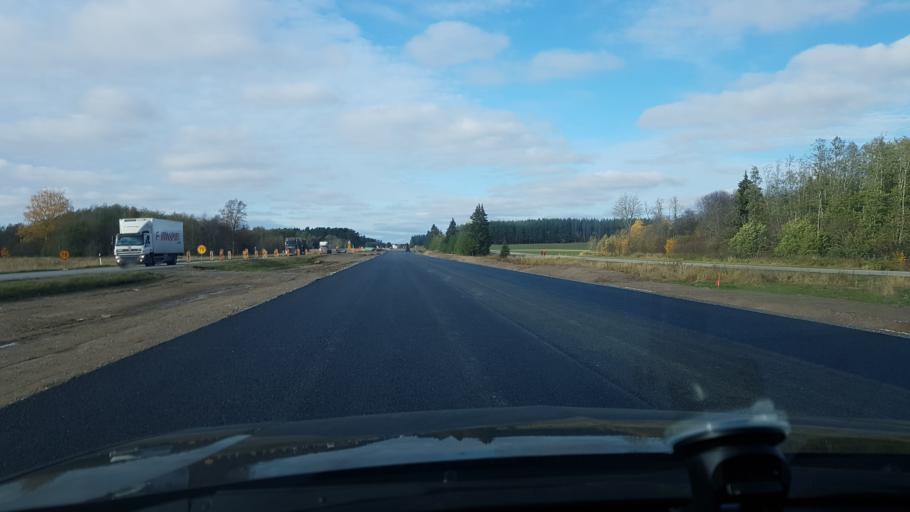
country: EE
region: Laeaene-Virumaa
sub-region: Kadrina vald
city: Kadrina
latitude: 59.4437
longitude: 26.1005
